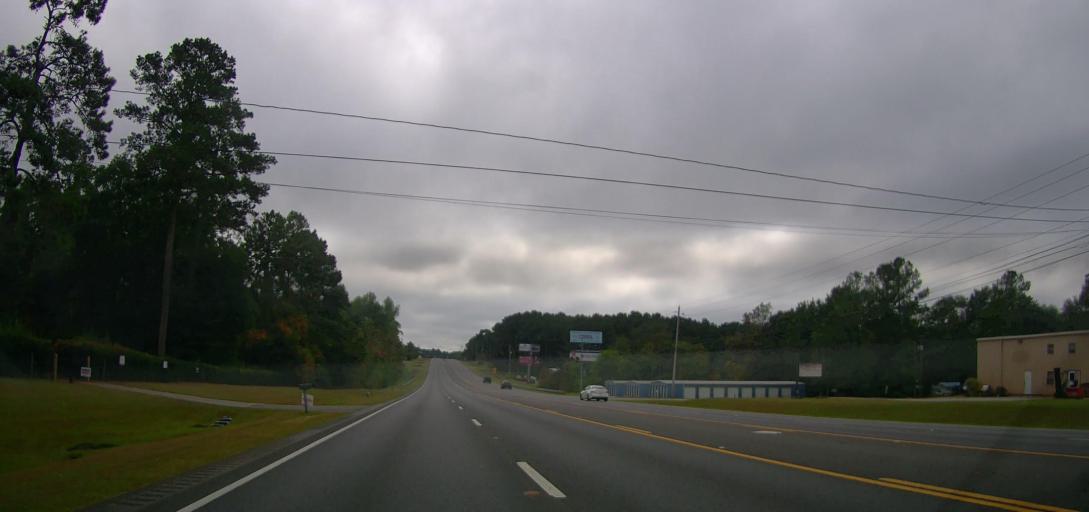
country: US
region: Georgia
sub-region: Thomas County
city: Thomasville
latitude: 30.8903
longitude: -83.9321
